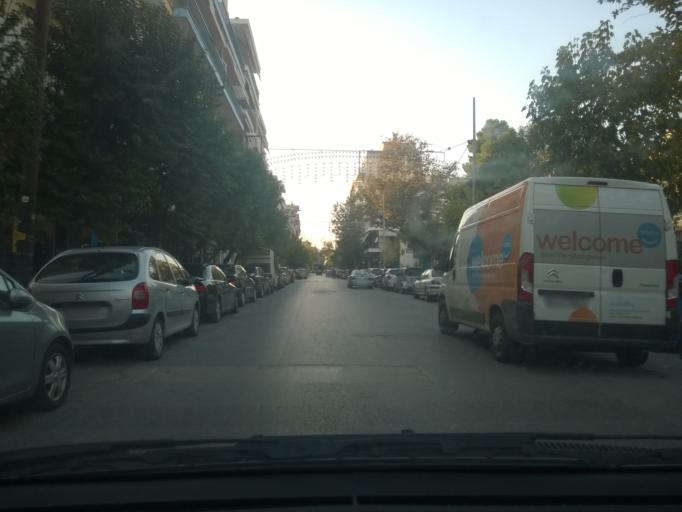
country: GR
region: Central Macedonia
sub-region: Nomos Thessalonikis
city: Ampelokipoi
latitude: 40.6536
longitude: 22.9252
